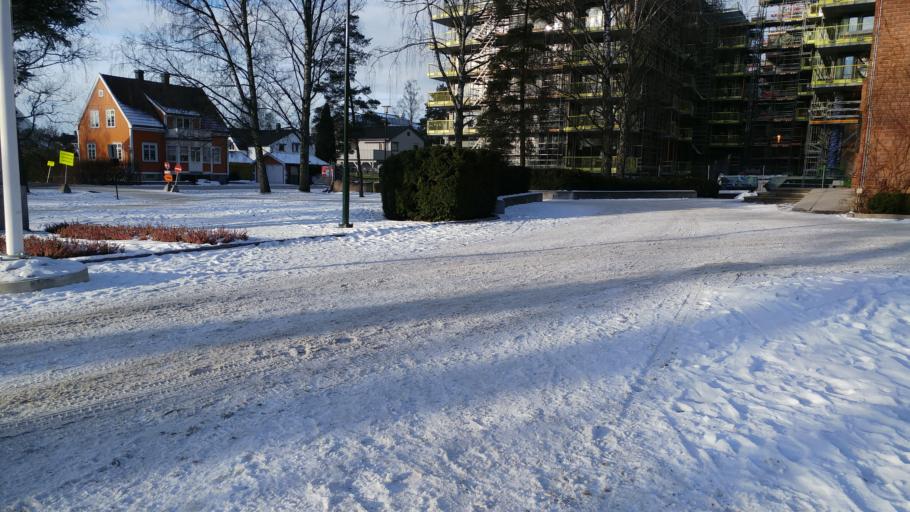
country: NO
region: Akershus
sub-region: Skedsmo
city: Lillestrom
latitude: 59.9584
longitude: 11.0479
